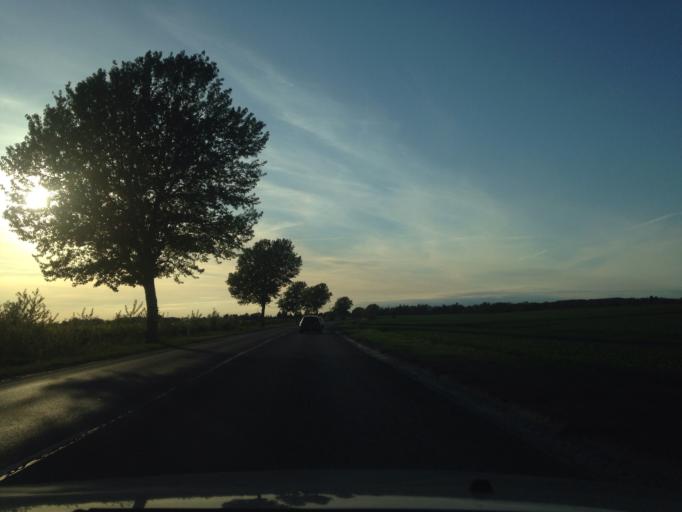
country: DK
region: Zealand
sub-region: Greve Kommune
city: Tune
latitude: 55.5918
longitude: 12.2410
